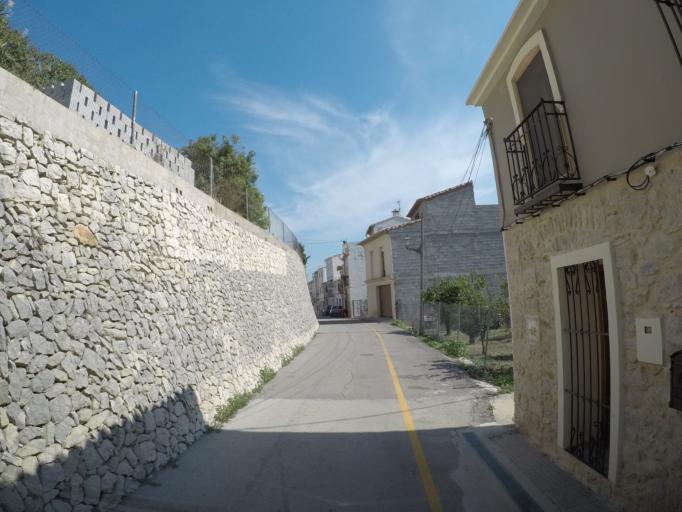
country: ES
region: Valencia
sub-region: Provincia de Alicante
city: Murla
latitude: 38.7786
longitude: -0.1048
